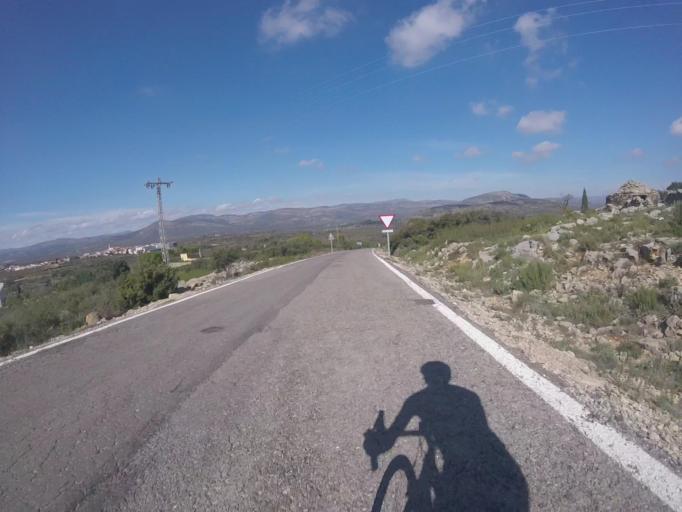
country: ES
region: Valencia
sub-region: Provincia de Castello
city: Albocasser
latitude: 40.3560
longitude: 0.0386
